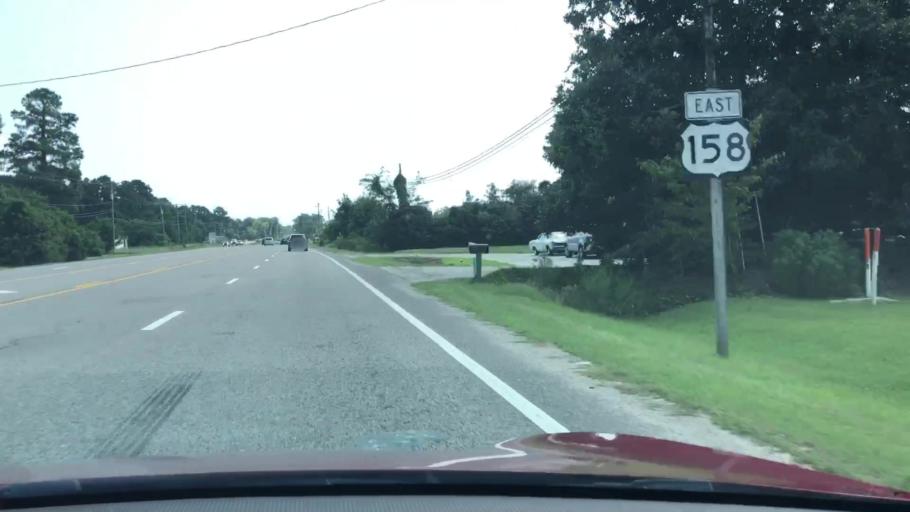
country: US
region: North Carolina
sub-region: Dare County
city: Southern Shores
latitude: 36.1196
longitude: -75.8322
